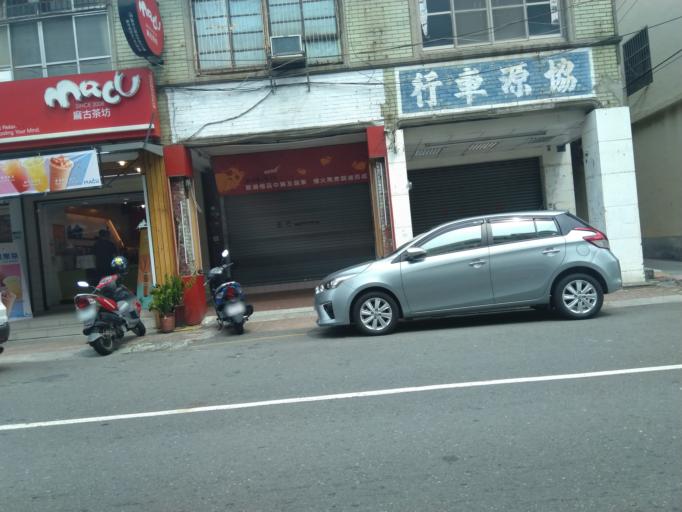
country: TW
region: Kaohsiung
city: Kaohsiung
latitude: 22.6834
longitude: 120.2889
